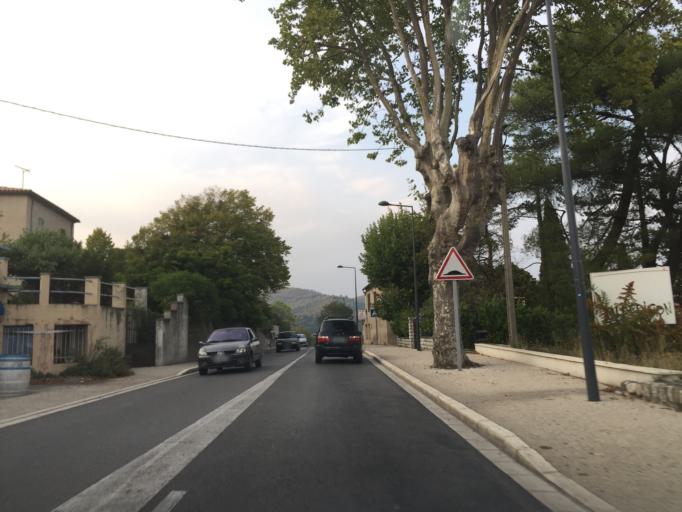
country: FR
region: Provence-Alpes-Cote d'Azur
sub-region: Departement des Alpes-de-Haute-Provence
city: Volx
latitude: 43.8754
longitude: 5.8435
